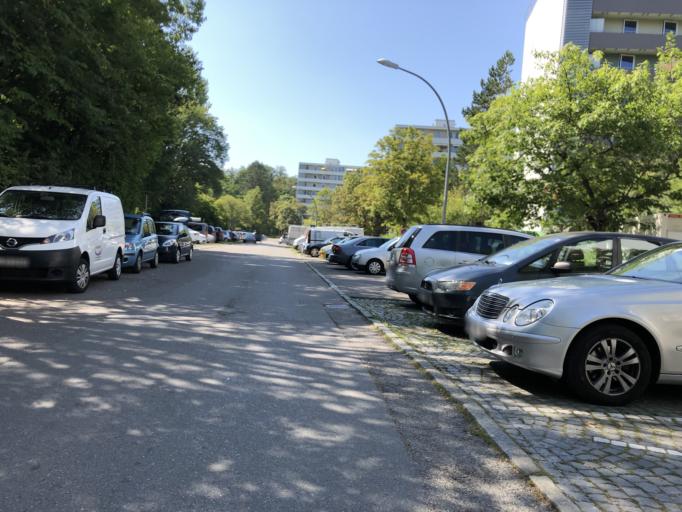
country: DE
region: Baden-Wuerttemberg
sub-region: Regierungsbezirk Stuttgart
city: Magstadt
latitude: 48.7315
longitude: 9.0015
